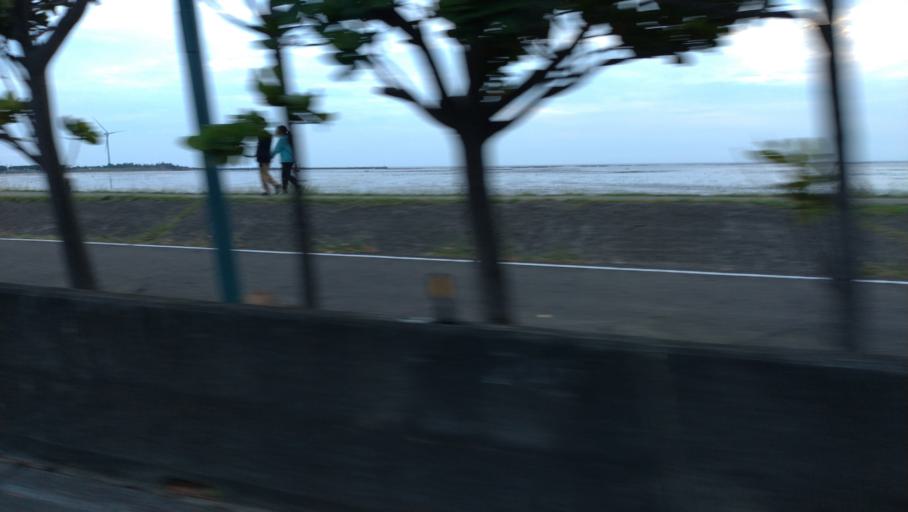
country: TW
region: Taiwan
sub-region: Hsinchu
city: Hsinchu
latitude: 24.7715
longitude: 120.9137
